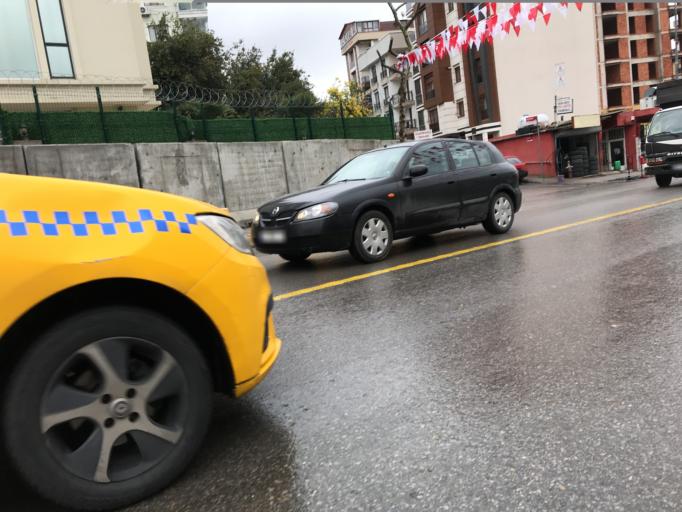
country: TR
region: Istanbul
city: Maltepe
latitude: 40.9392
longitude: 29.1418
